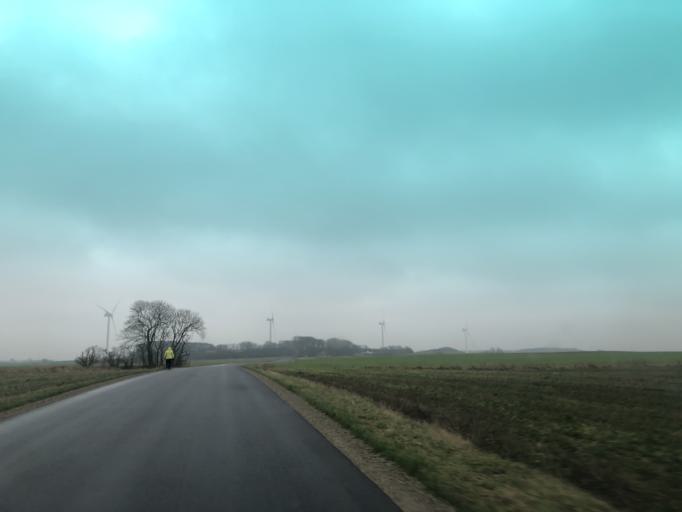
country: DK
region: Central Jutland
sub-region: Struer Kommune
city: Struer
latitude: 56.4327
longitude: 8.5894
